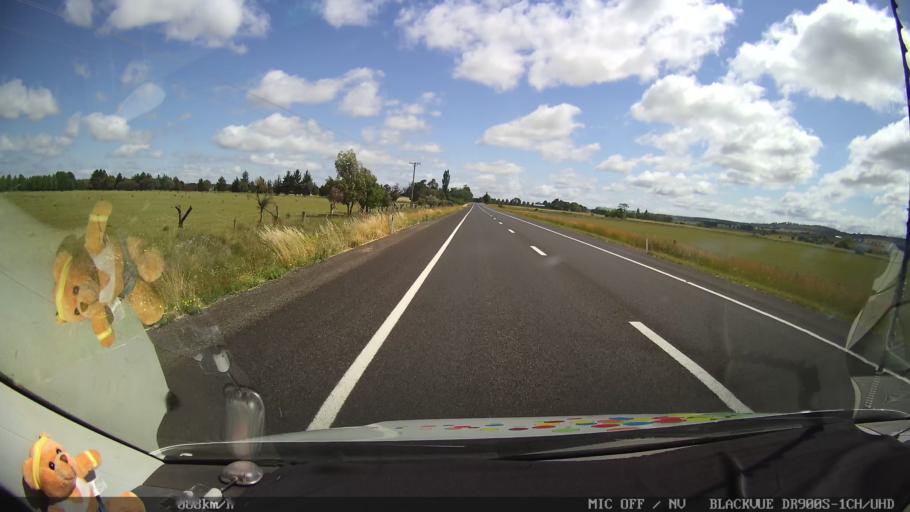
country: AU
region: New South Wales
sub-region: Glen Innes Severn
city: Glen Innes
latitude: -29.8266
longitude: 151.7388
